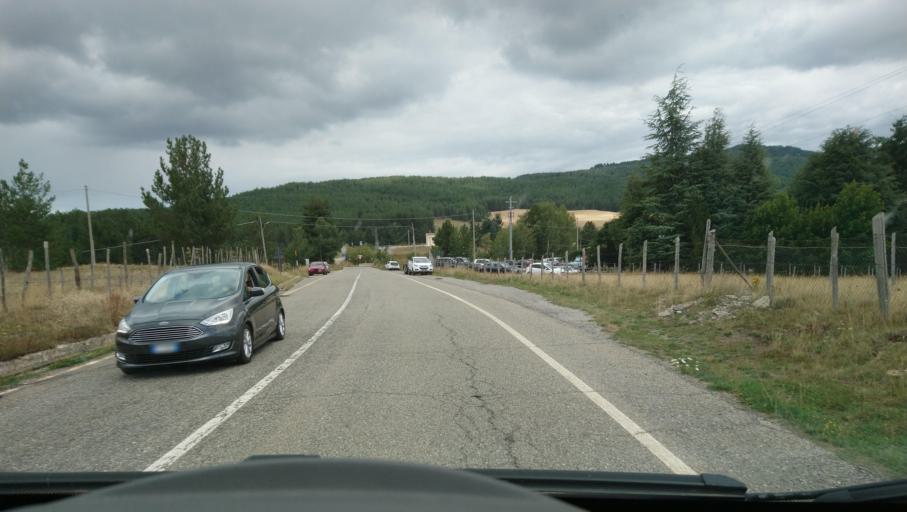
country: IT
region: Calabria
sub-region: Provincia di Cosenza
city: Longobucco
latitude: 39.3134
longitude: 16.5434
